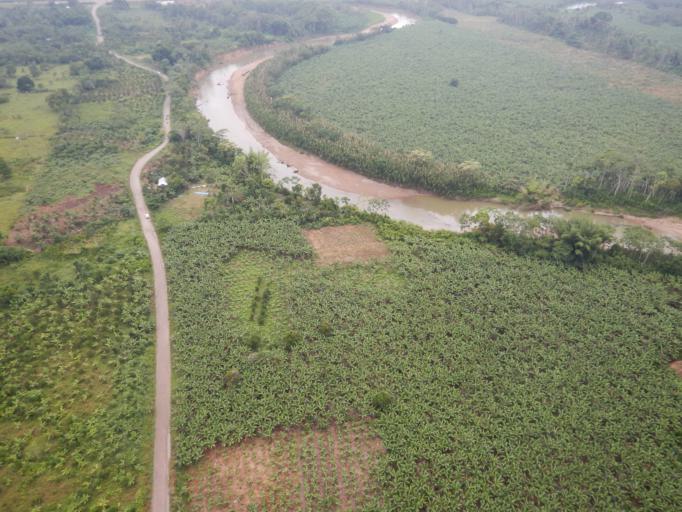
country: BO
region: Cochabamba
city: Chimore
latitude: -17.1437
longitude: -64.7011
